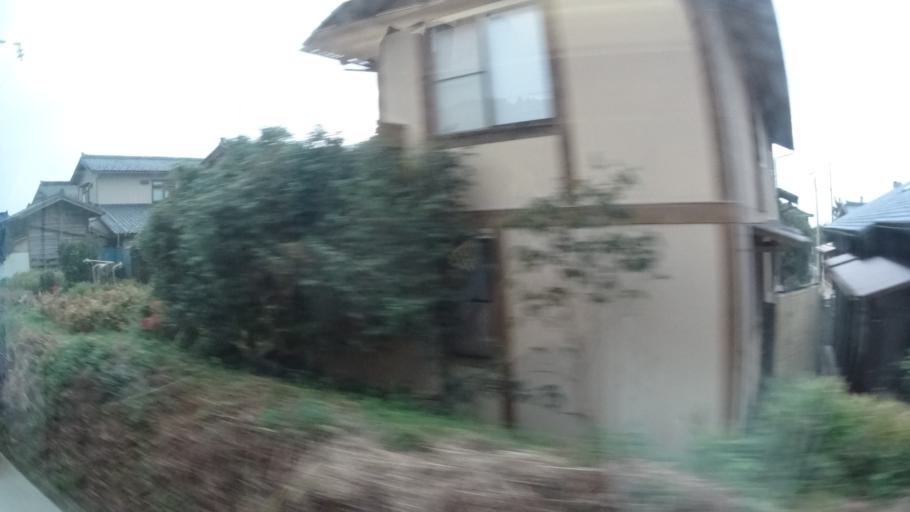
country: JP
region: Niigata
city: Murakami
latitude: 38.2776
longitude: 139.4509
